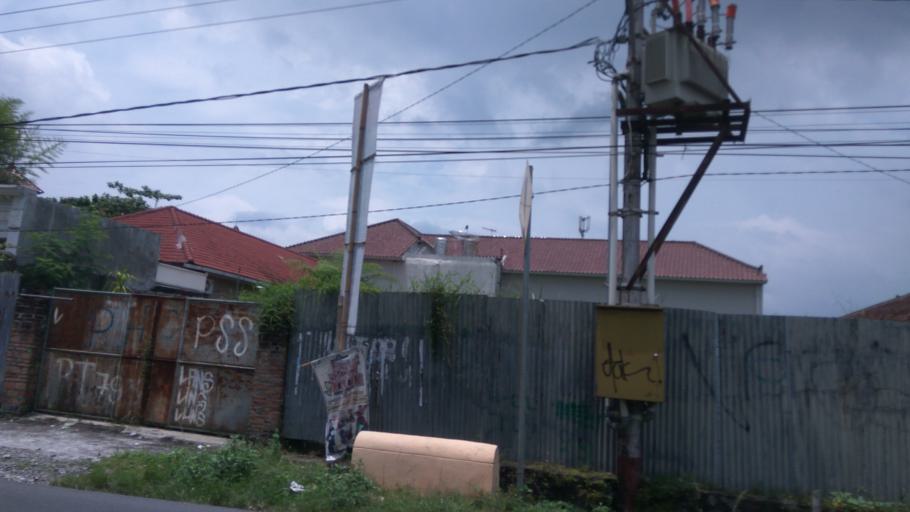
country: ID
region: Daerah Istimewa Yogyakarta
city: Melati
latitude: -7.7290
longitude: 110.3797
